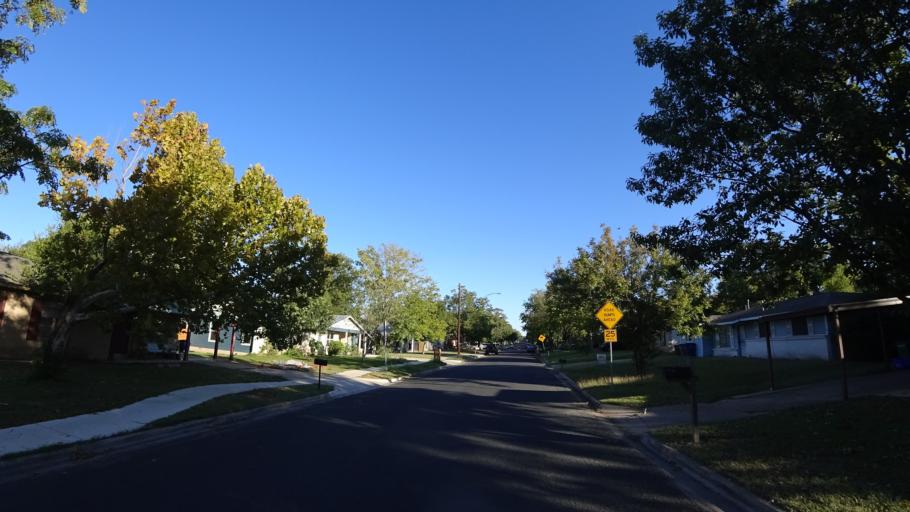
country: US
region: Texas
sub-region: Travis County
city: Austin
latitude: 30.3015
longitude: -97.6854
